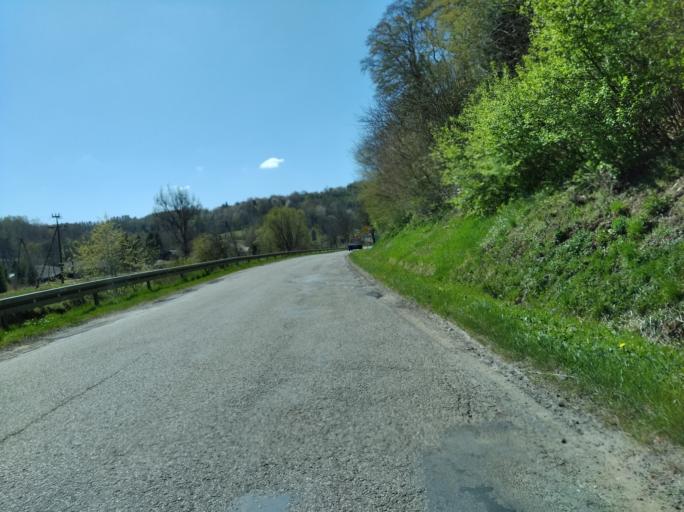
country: PL
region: Subcarpathian Voivodeship
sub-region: Powiat brzozowski
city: Dydnia
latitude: 49.6995
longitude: 22.1929
